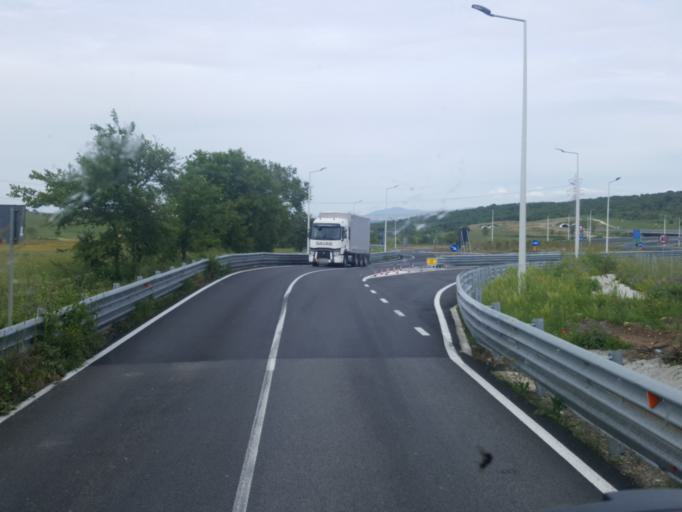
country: IT
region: Latium
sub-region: Provincia di Viterbo
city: Monte Romano
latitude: 42.2815
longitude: 11.9217
